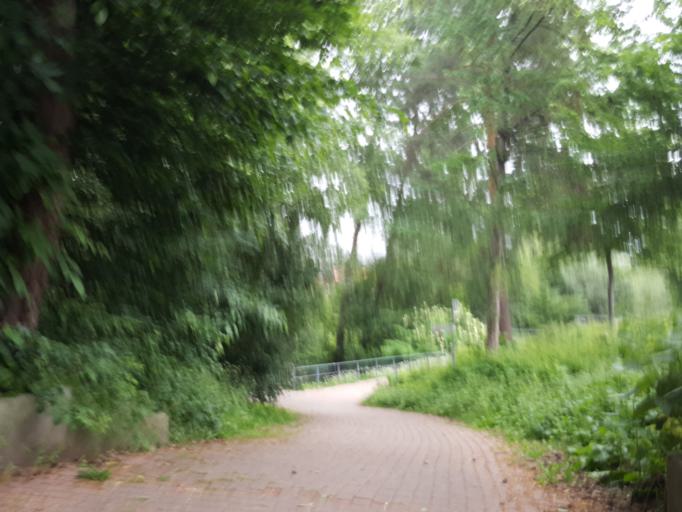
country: DE
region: Hamburg
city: Wandsbek
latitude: 53.5392
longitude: 10.1165
